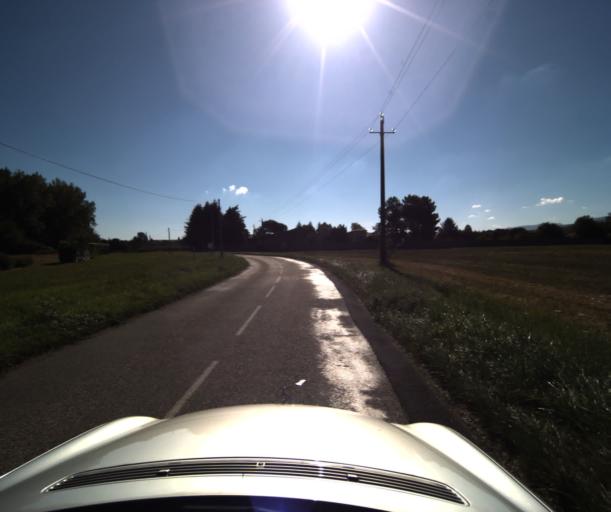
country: FR
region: Midi-Pyrenees
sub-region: Departement de l'Ariege
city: Lavelanet
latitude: 42.9885
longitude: 1.8982
